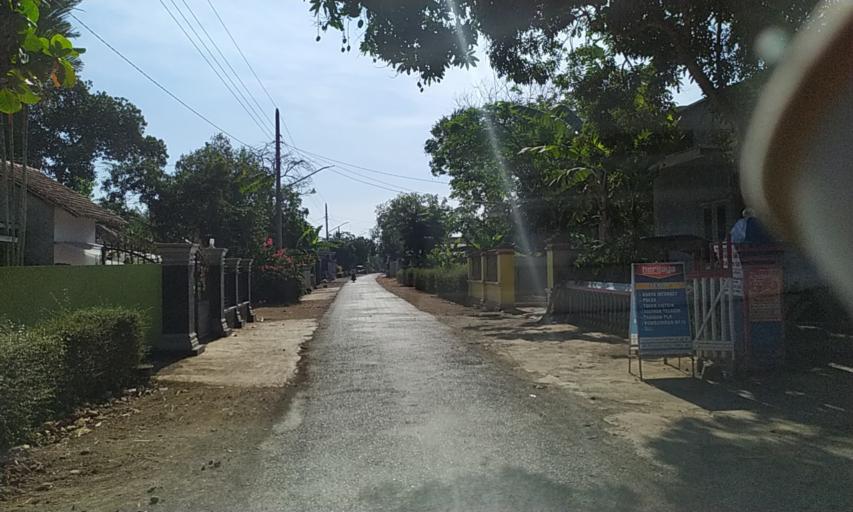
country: ID
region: Central Java
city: Kroya
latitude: -7.6470
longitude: 109.3026
